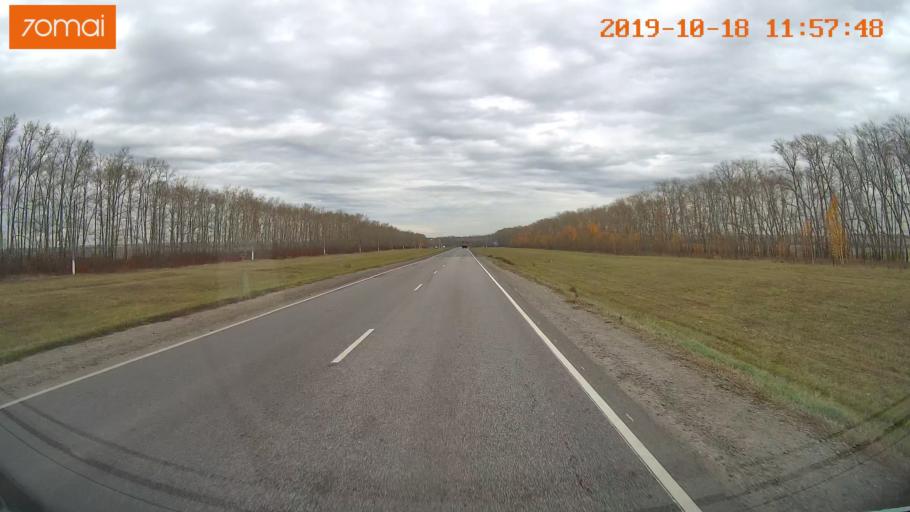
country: RU
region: Rjazan
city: Mikhaylov
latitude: 54.2674
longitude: 39.1536
